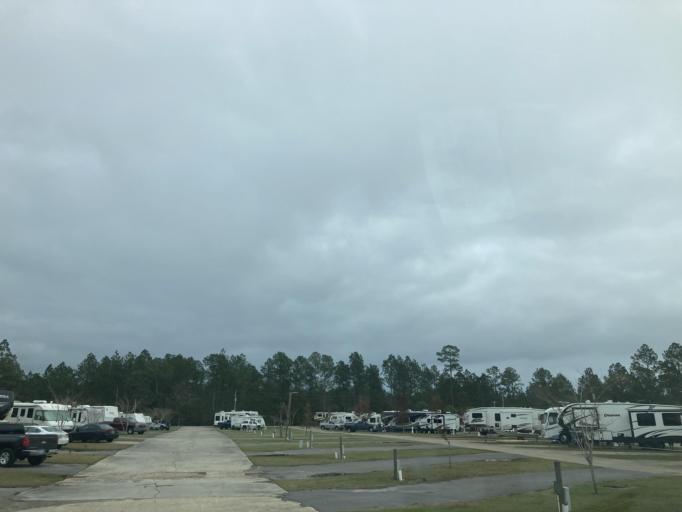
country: US
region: Mississippi
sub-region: Jackson County
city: Latimer
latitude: 30.5383
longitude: -88.9235
